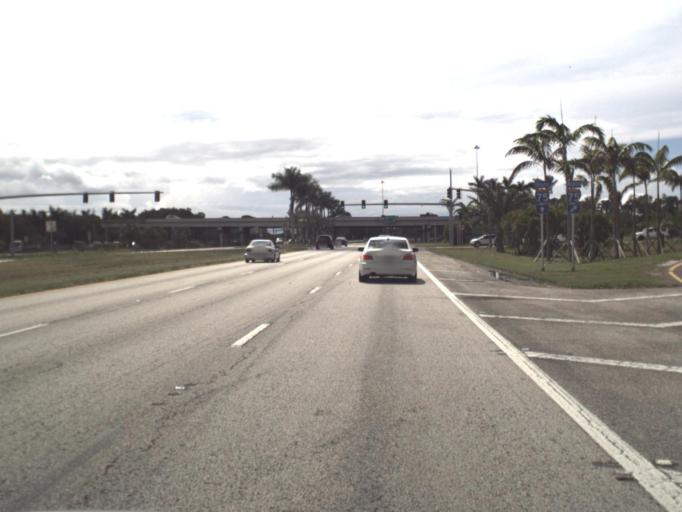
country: US
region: Florida
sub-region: Manatee County
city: Ellenton
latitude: 27.5308
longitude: -82.5051
